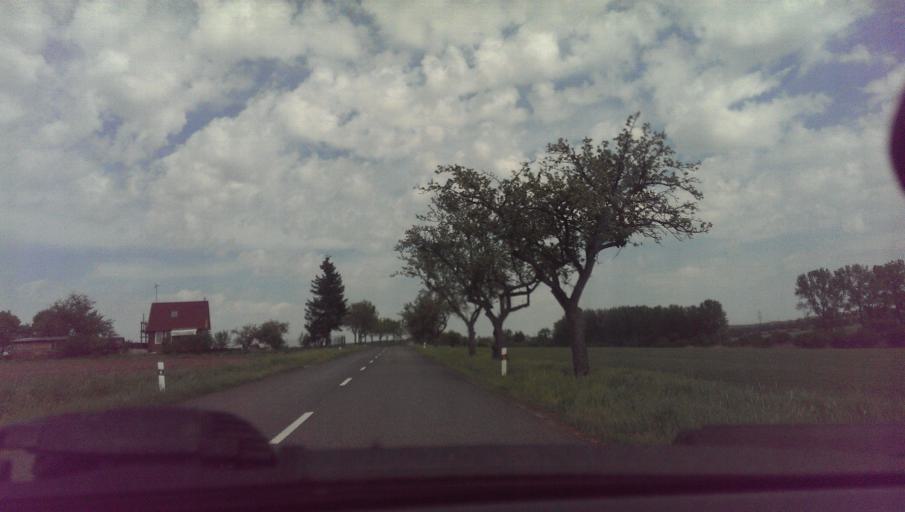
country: CZ
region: Zlin
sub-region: Okres Zlin
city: Otrokovice
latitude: 49.2249
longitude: 17.5362
